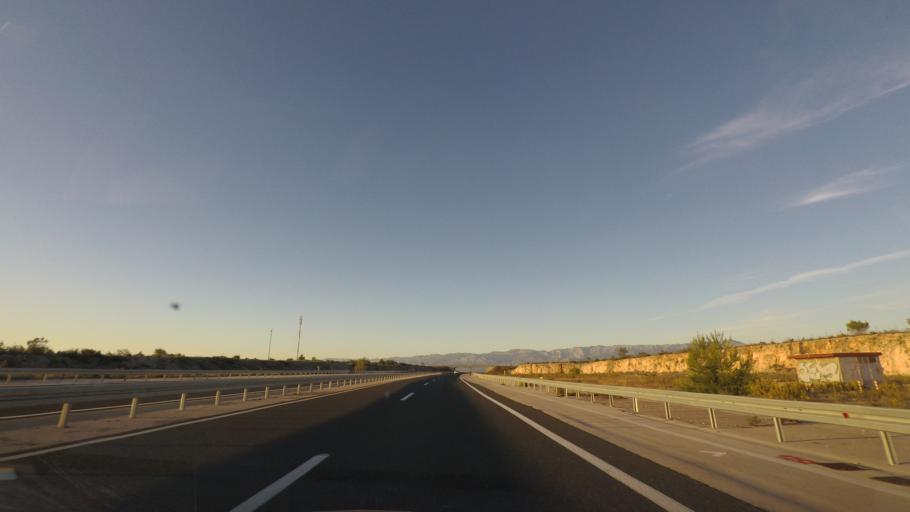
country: HR
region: Zadarska
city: Policnik
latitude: 44.1370
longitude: 15.4206
